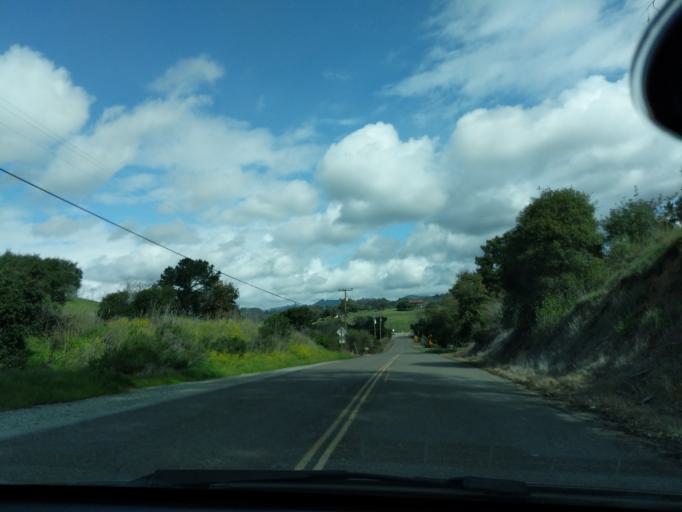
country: US
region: California
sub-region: San Benito County
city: Aromas
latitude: 36.8510
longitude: -121.6397
